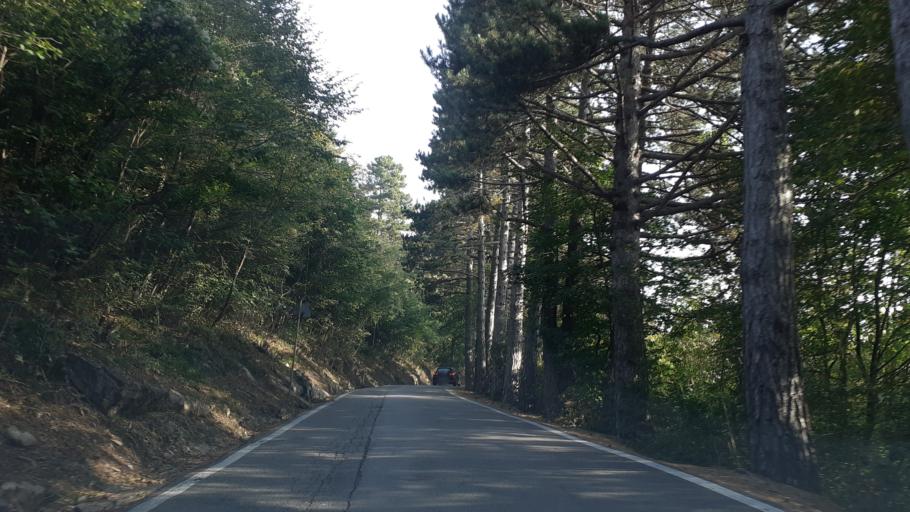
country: IT
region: Lombardy
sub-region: Provincia di Lecco
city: Ballabio
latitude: 45.8980
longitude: 9.4059
